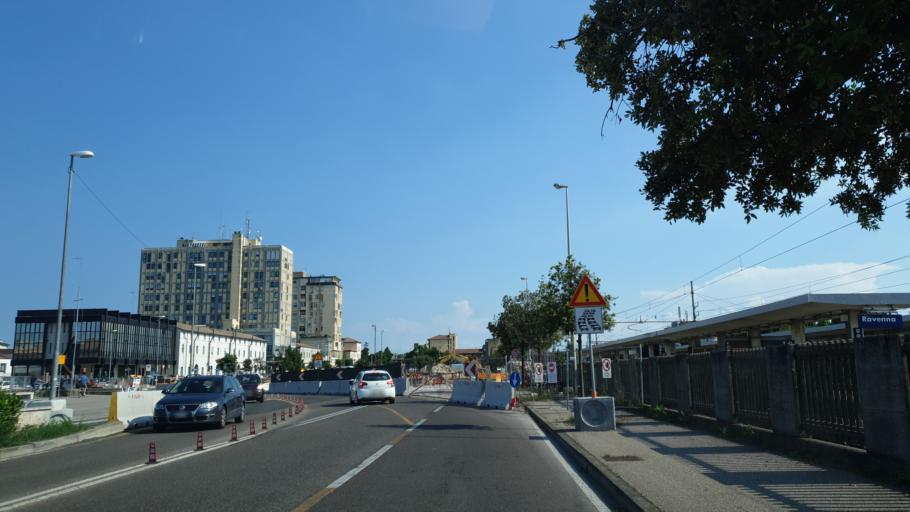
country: IT
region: Emilia-Romagna
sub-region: Provincia di Ravenna
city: Ravenna
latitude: 44.4200
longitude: 12.2087
